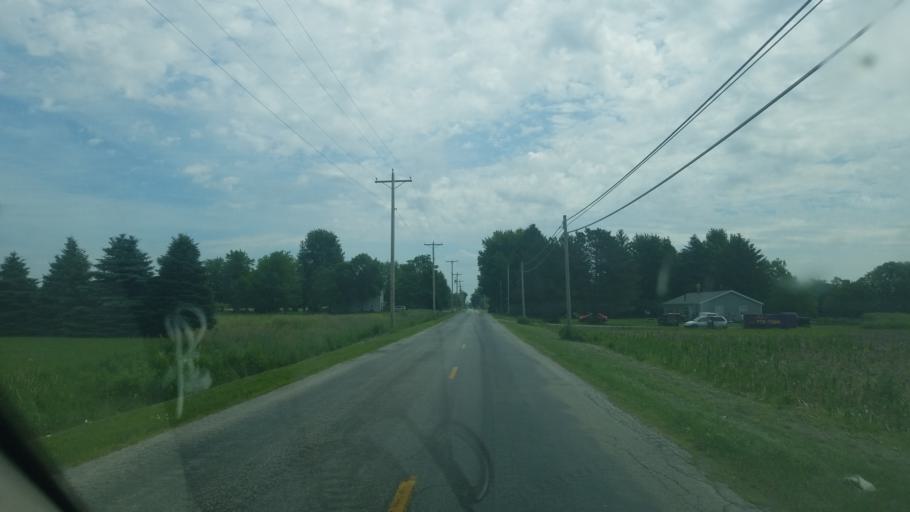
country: US
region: Ohio
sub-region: Wood County
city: Bowling Green
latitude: 41.2975
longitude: -83.6586
